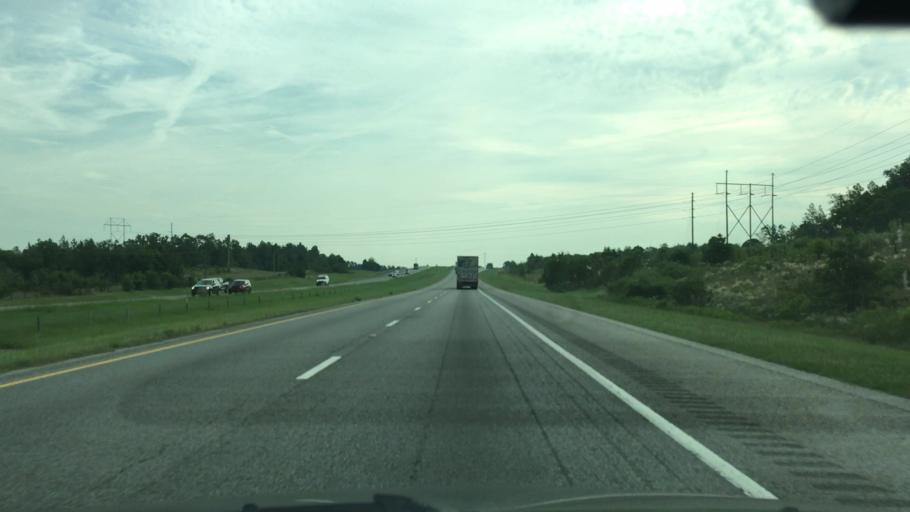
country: US
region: South Carolina
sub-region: Lexington County
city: Batesburg
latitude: 33.7166
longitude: -81.5748
